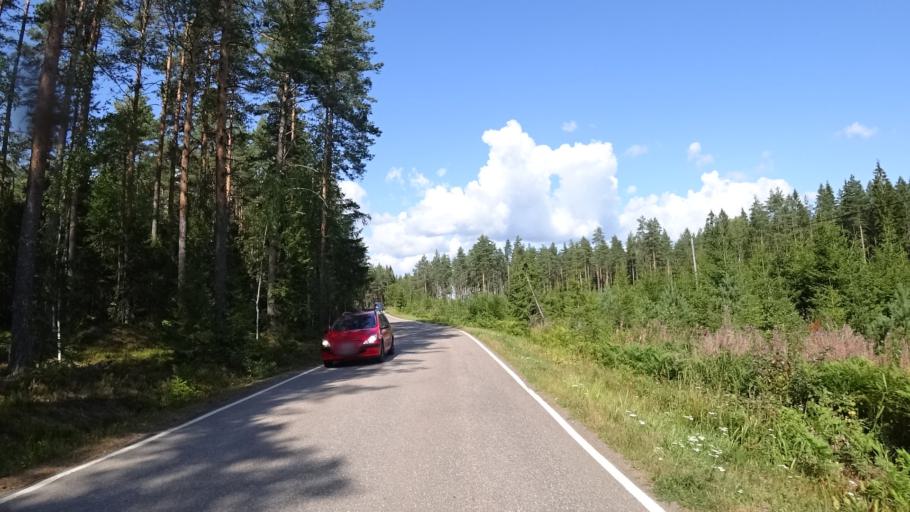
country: FI
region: Kymenlaakso
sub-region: Kotka-Hamina
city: Karhula
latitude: 60.5644
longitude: 26.9008
